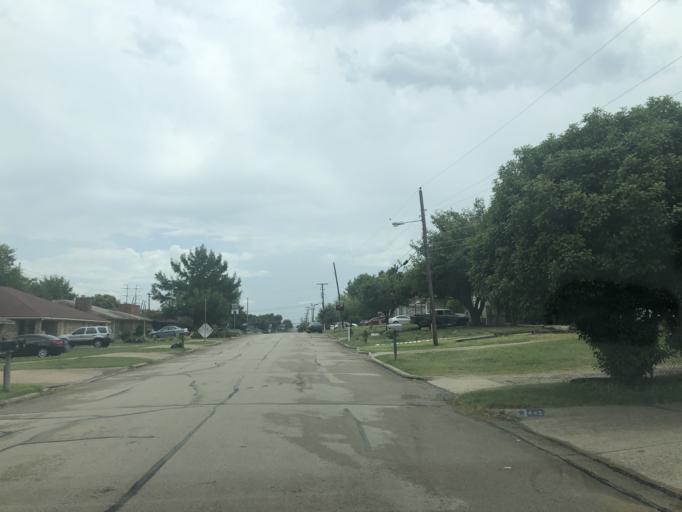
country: US
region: Texas
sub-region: Dallas County
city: Grand Prairie
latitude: 32.7464
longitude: -97.0355
